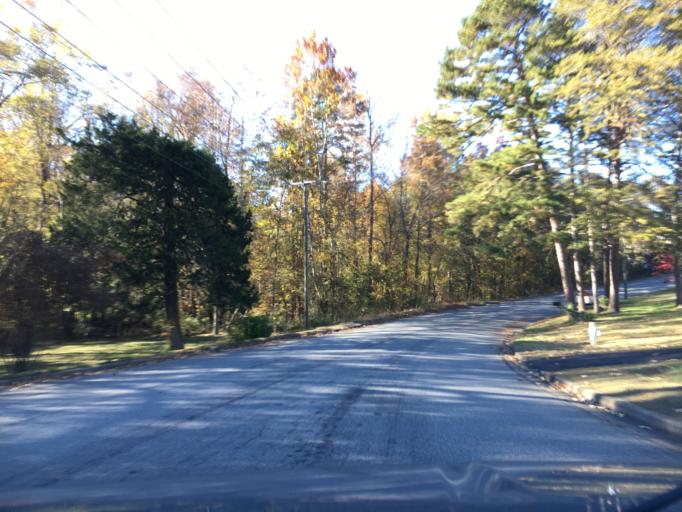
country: US
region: Virginia
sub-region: Halifax County
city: South Boston
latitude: 36.7030
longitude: -78.8869
